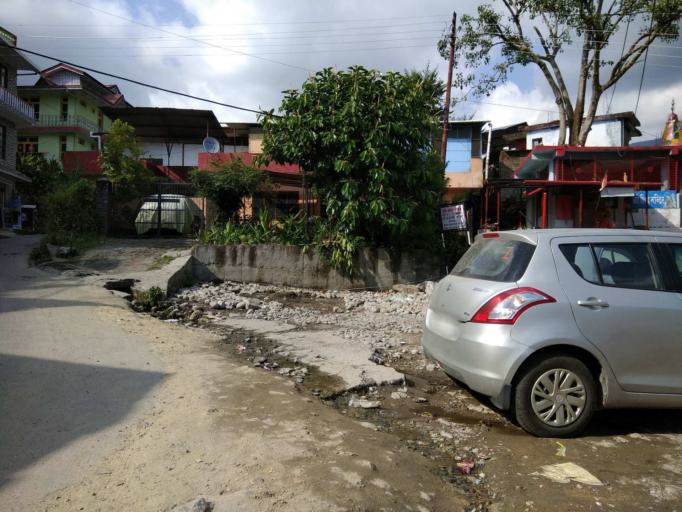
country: IN
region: Himachal Pradesh
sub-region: Kangra
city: Palampur
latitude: 32.1148
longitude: 76.5347
